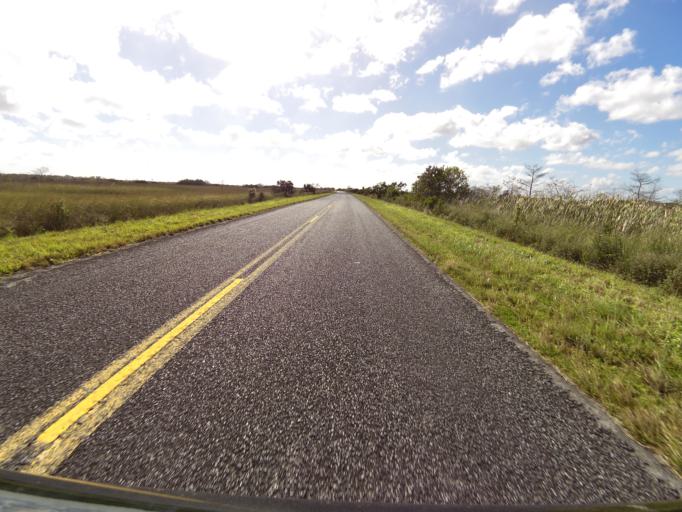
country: US
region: Florida
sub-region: Miami-Dade County
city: Florida City
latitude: 25.3868
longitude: -80.8063
